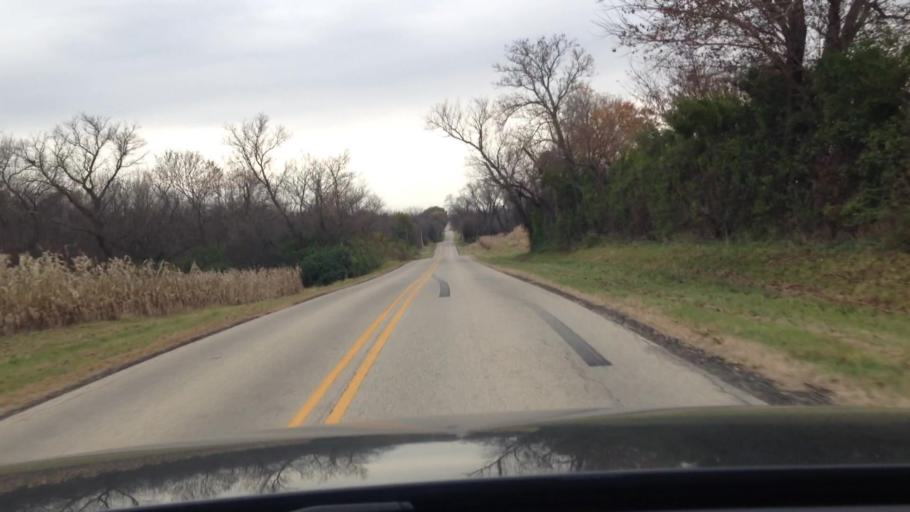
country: US
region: Illinois
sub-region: McHenry County
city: Woodstock
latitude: 42.2919
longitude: -88.4771
